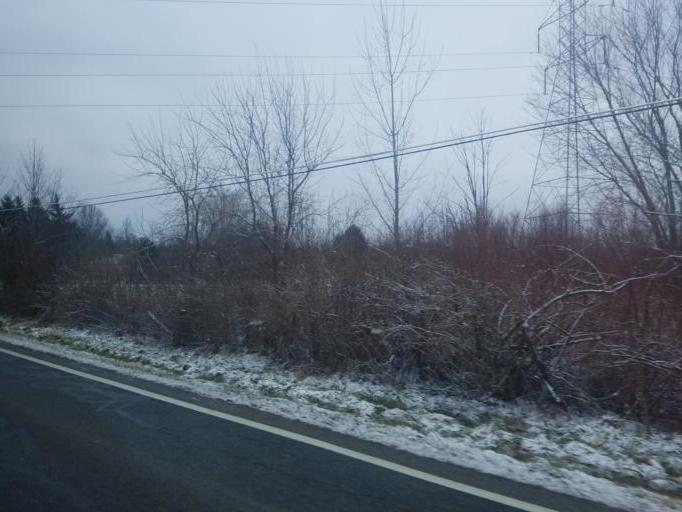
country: US
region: Ohio
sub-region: Franklin County
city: New Albany
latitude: 40.0395
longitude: -82.7879
